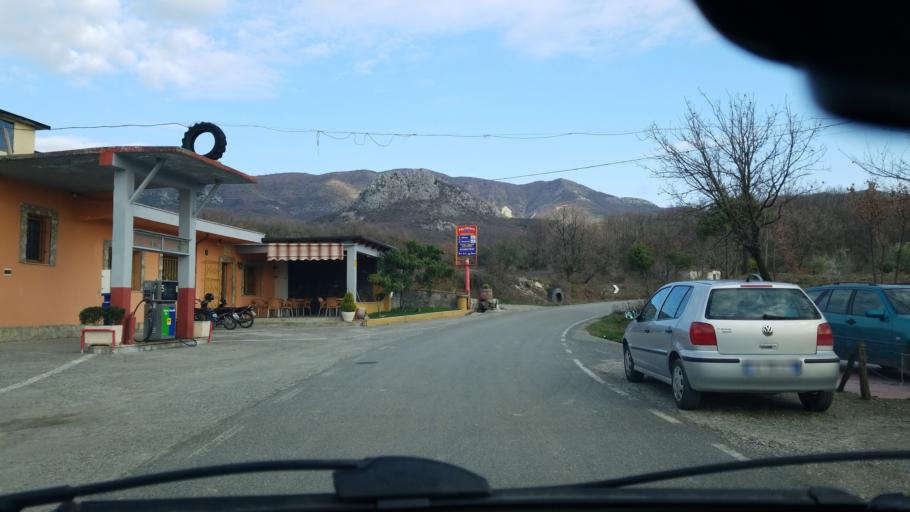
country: AL
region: Lezhe
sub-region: Rrethi i Lezhes
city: Kallmeti i Madh
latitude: 41.8834
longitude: 19.6904
